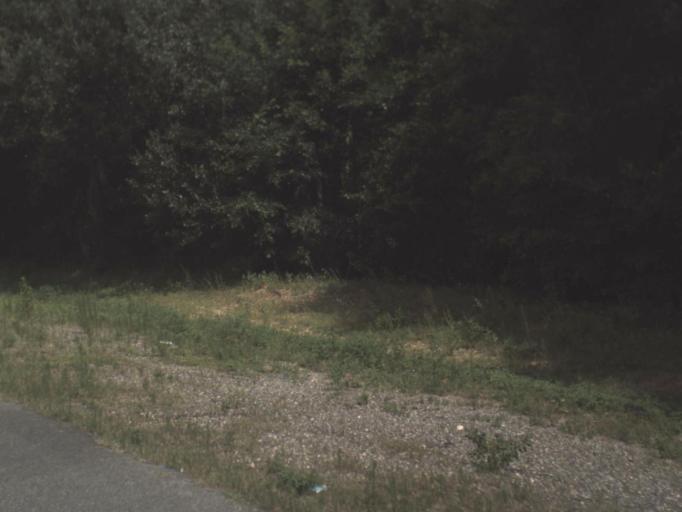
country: US
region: Florida
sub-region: Madison County
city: Madison
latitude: 30.4845
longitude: -83.4538
